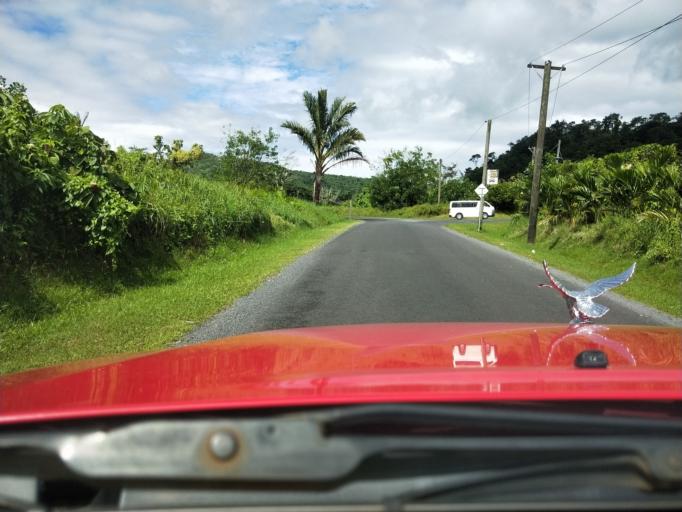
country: WS
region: Va`a-o-Fonoti
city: Samamea
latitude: -13.9643
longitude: -171.5820
